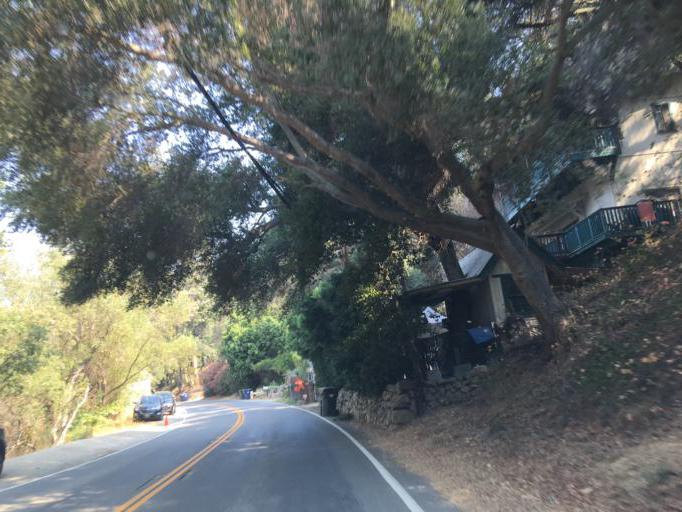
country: US
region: California
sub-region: Los Angeles County
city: Topanga
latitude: 34.0984
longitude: -118.6173
